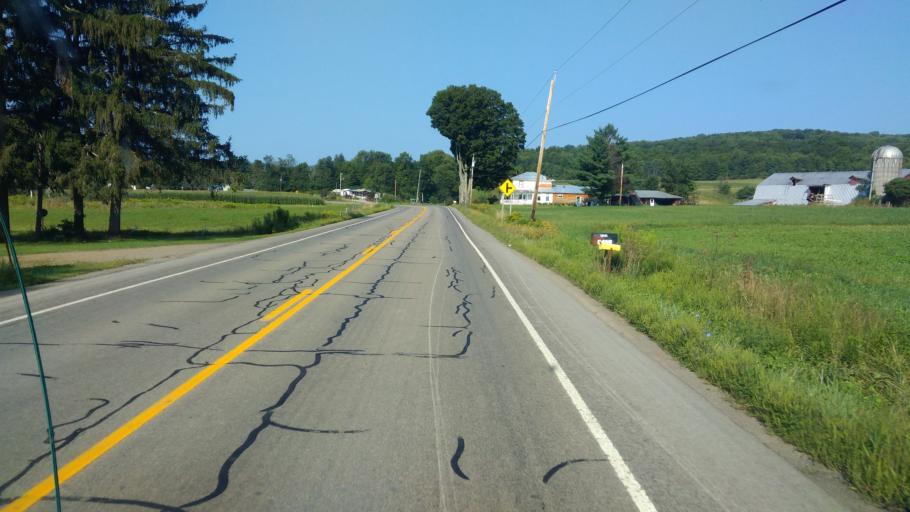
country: US
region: New York
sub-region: Allegany County
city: Friendship
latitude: 42.3047
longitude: -78.1758
